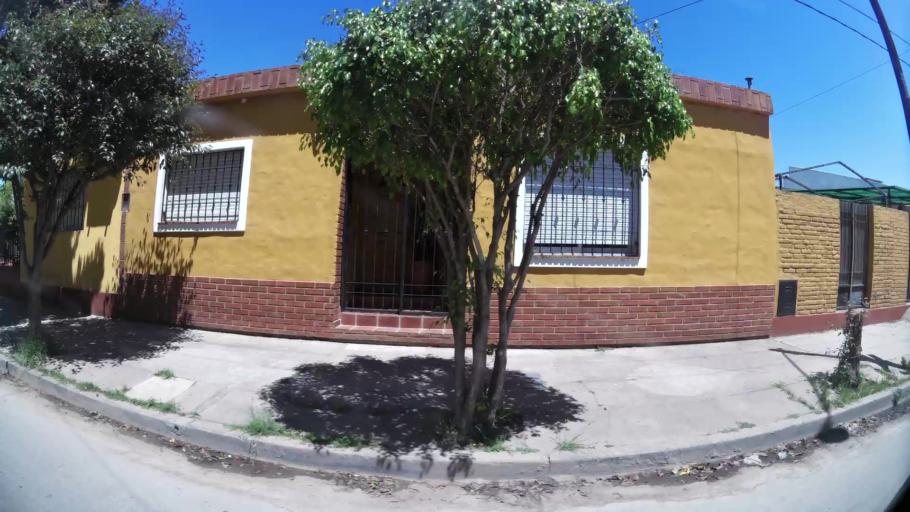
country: AR
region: Cordoba
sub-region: Departamento de Capital
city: Cordoba
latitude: -31.4352
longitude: -64.1272
